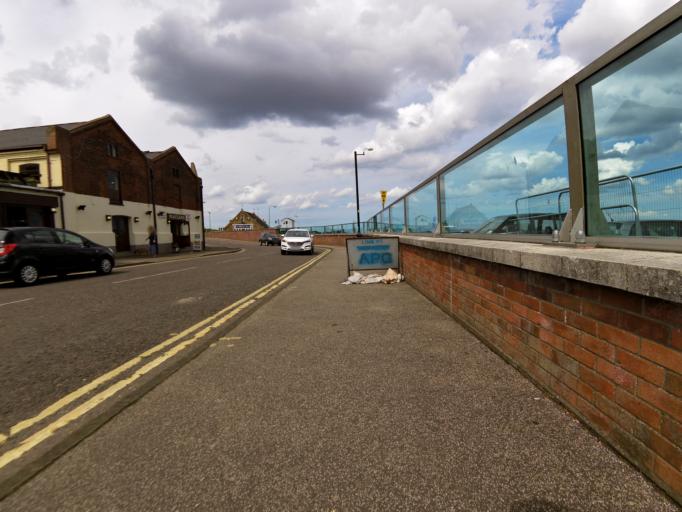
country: GB
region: England
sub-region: Norfolk
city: Wells-next-the-Sea
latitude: 52.9576
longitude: 0.8508
